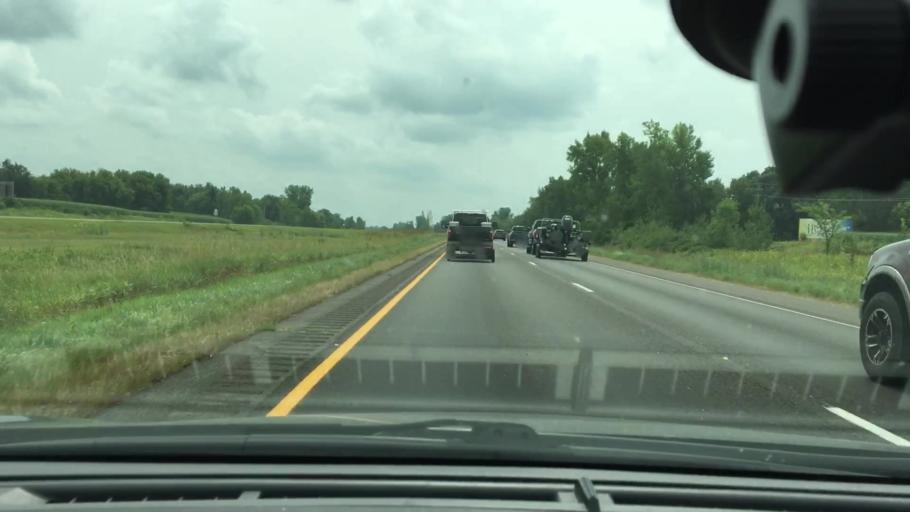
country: US
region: Minnesota
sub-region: Mille Lacs County
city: Princeton
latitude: 45.6200
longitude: -93.6128
